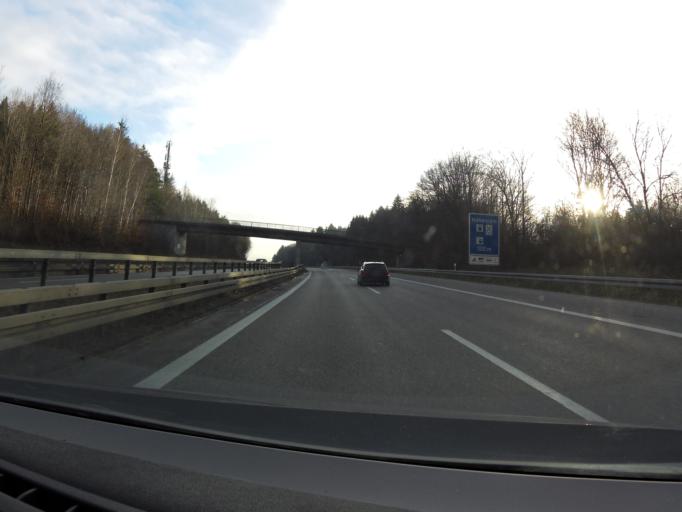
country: DE
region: Bavaria
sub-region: Upper Bavaria
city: Wolfratshausen
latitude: 47.9363
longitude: 11.4025
